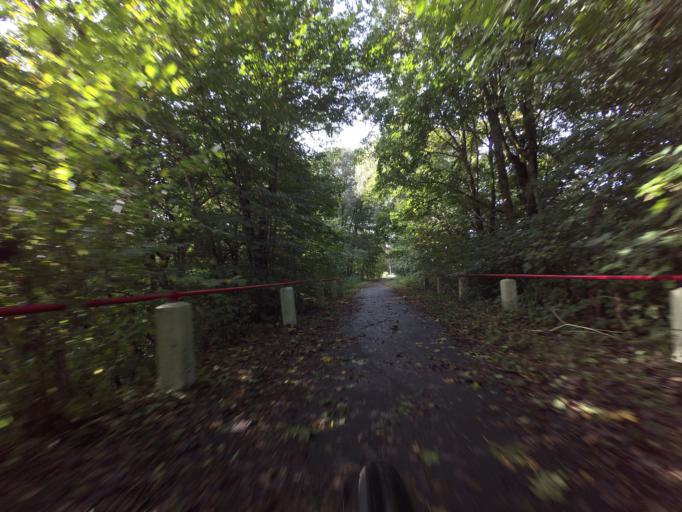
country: DK
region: Central Jutland
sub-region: Viborg Kommune
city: Viborg
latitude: 56.4231
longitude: 9.4516
